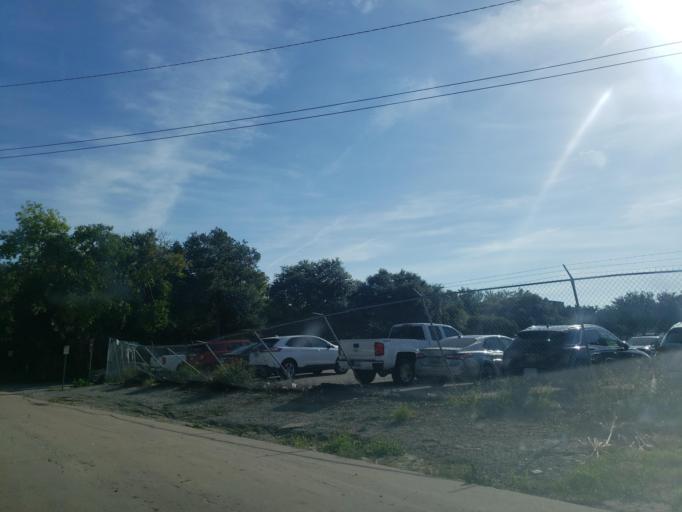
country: US
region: Georgia
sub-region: Chatham County
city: Savannah
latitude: 32.0805
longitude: -81.0985
